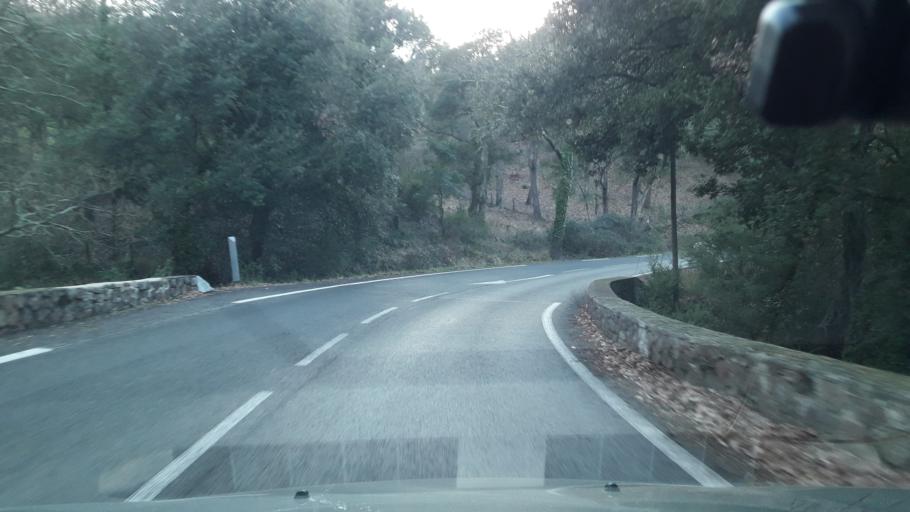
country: FR
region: Provence-Alpes-Cote d'Azur
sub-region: Departement du Var
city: Tanneron
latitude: 43.5161
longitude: 6.8368
